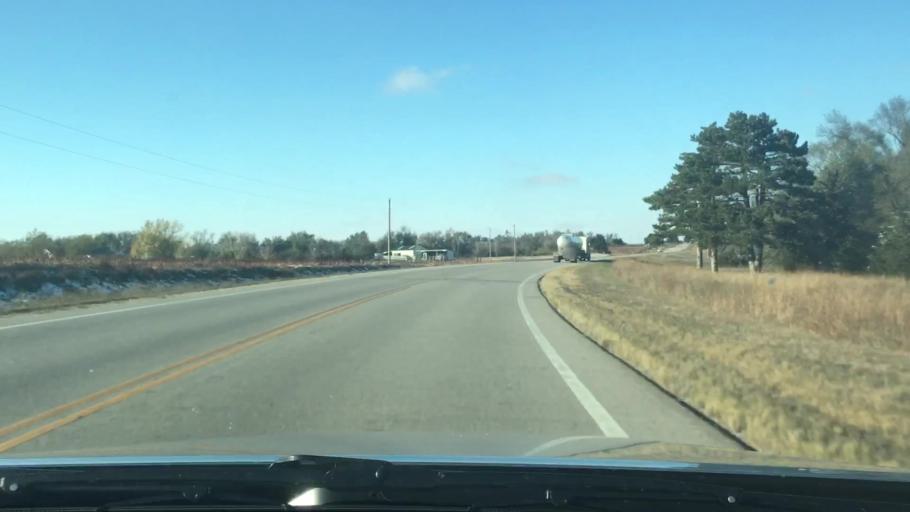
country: US
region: Kansas
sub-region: Rice County
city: Sterling
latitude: 38.1465
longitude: -98.2027
